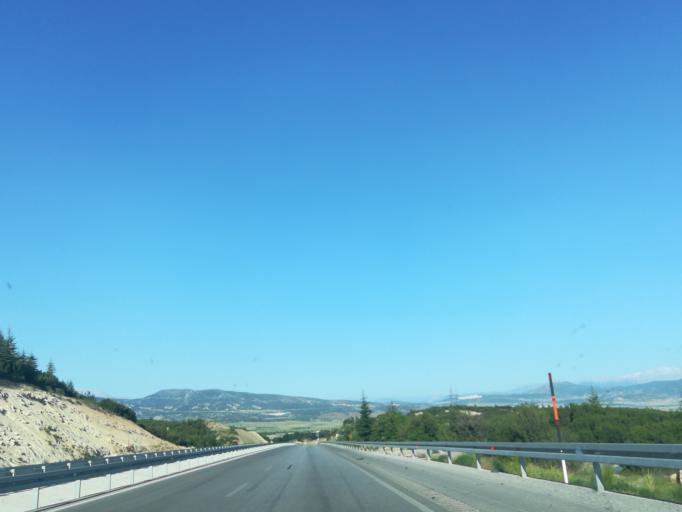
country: TR
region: Isparta
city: Keciborlu
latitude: 37.9160
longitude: 30.2853
